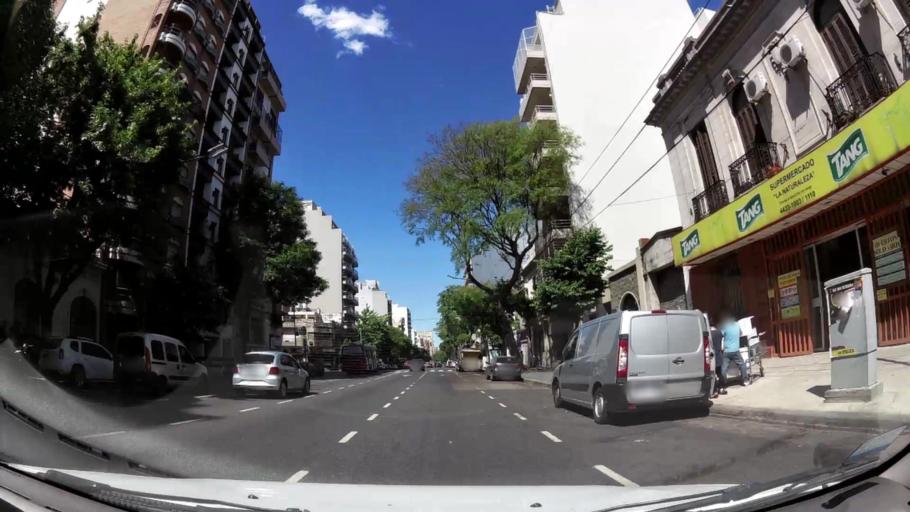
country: AR
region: Buenos Aires F.D.
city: Villa Santa Rita
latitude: -34.6299
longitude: -58.4467
